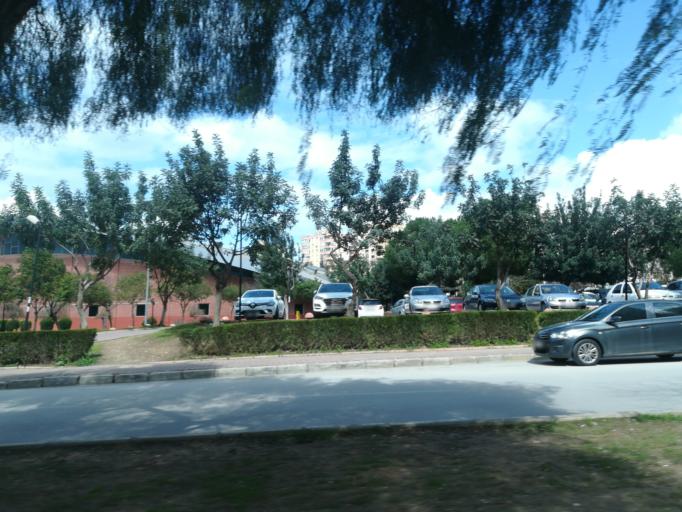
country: TR
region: Adana
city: Adana
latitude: 37.0359
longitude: 35.2956
